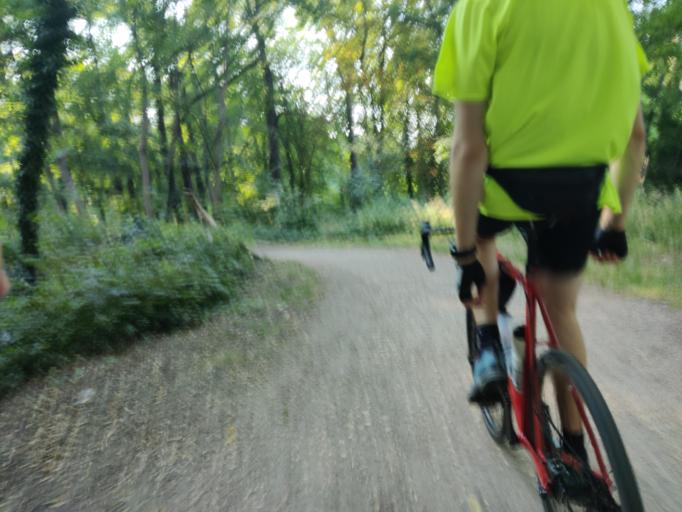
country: DE
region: Saxony
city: Rotha
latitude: 51.1972
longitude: 12.4073
